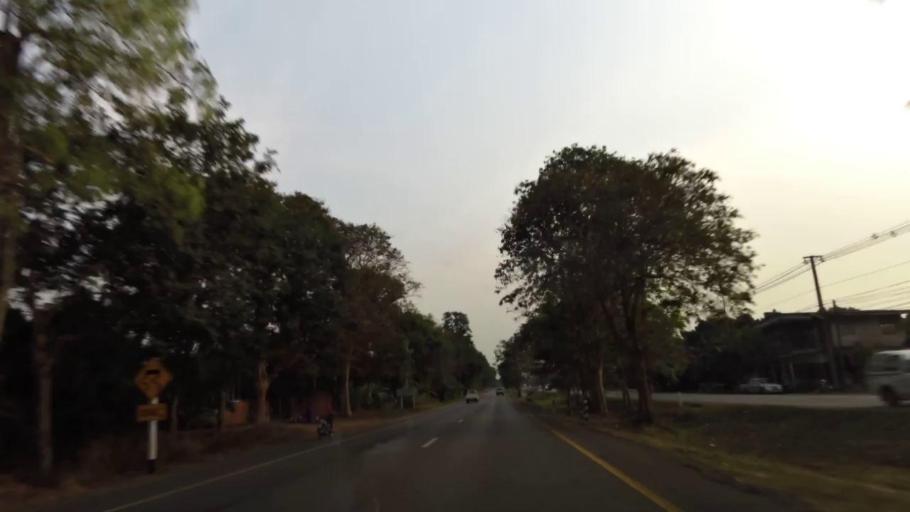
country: TH
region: Chanthaburi
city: Khlung
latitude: 12.4925
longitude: 102.1735
